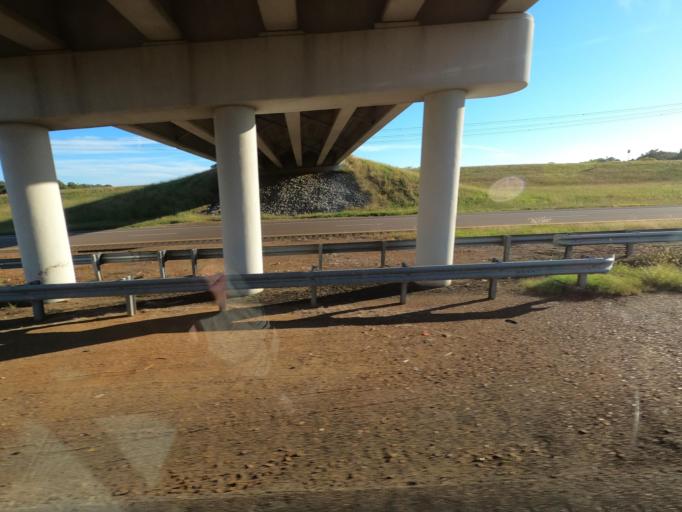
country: US
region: Tennessee
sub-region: Shelby County
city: Arlington
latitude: 35.3116
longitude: -89.7293
